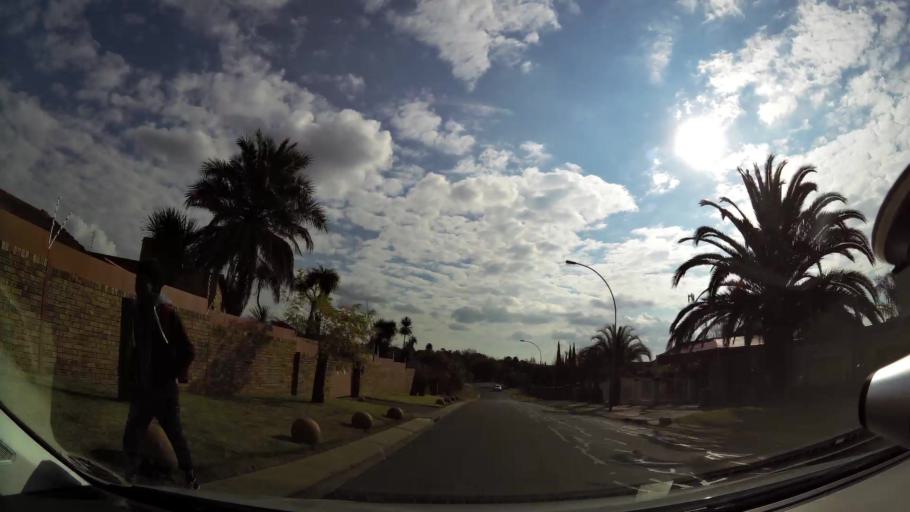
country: ZA
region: Orange Free State
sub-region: Mangaung Metropolitan Municipality
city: Bloemfontein
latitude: -29.0775
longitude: 26.2243
